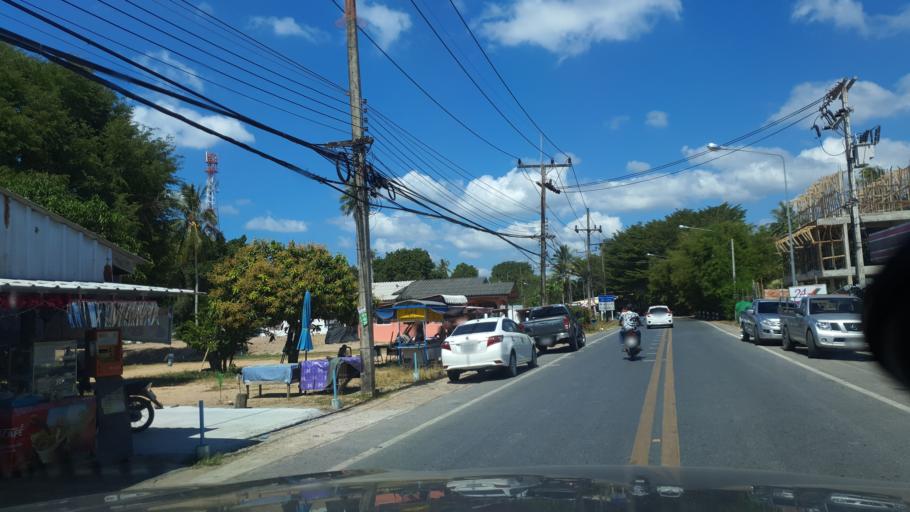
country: TH
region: Phuket
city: Thalang
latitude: 8.1289
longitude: 98.3080
